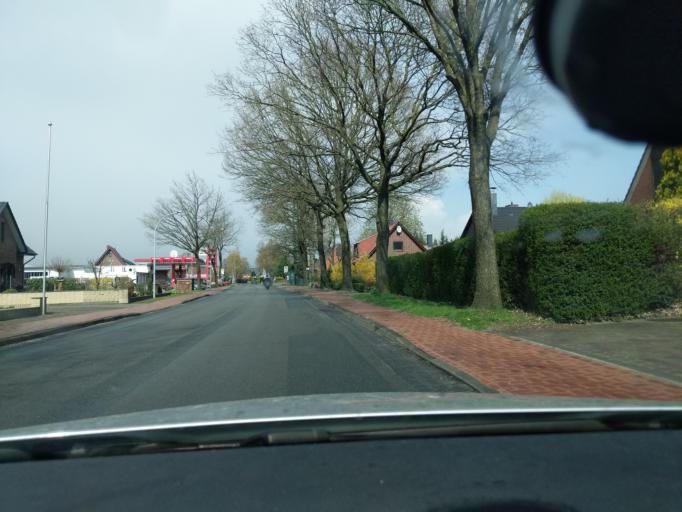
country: DE
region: Lower Saxony
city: Ahlerstedt
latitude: 53.4083
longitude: 9.4552
